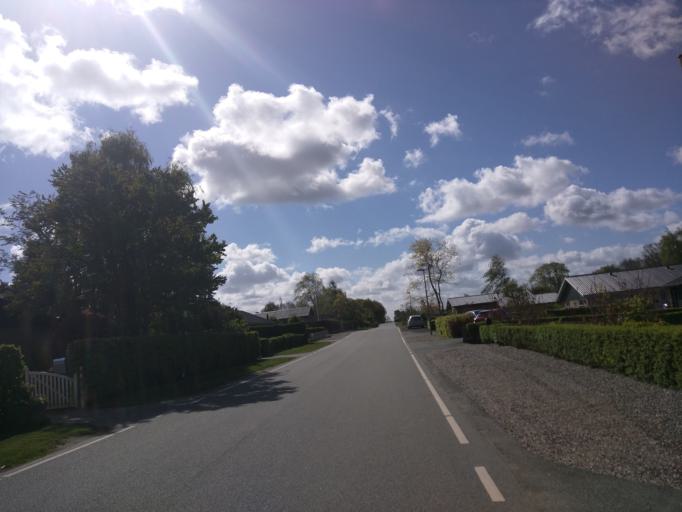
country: DK
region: Central Jutland
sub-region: Viborg Kommune
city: Viborg
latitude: 56.3969
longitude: 9.4379
